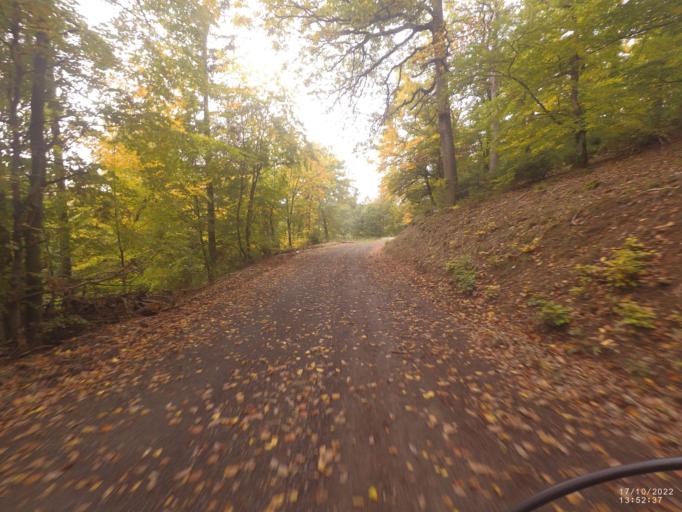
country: DE
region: Rheinland-Pfalz
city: Horscheid
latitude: 50.2154
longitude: 6.8453
